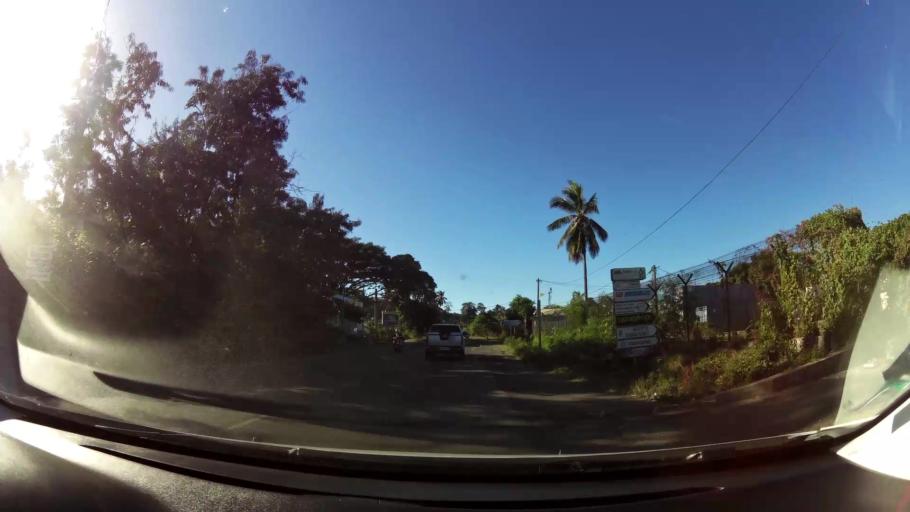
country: YT
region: Mamoudzou
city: Mamoudzou
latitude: -12.7642
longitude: 45.2256
